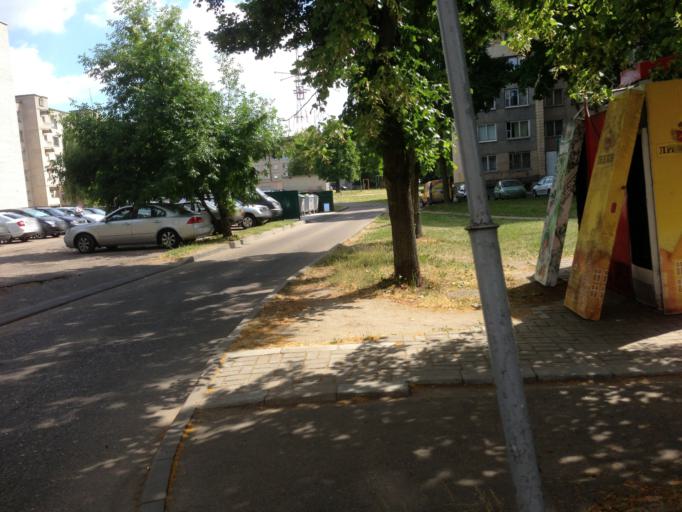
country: BY
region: Grodnenskaya
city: Hrodna
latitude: 53.6992
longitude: 23.8113
